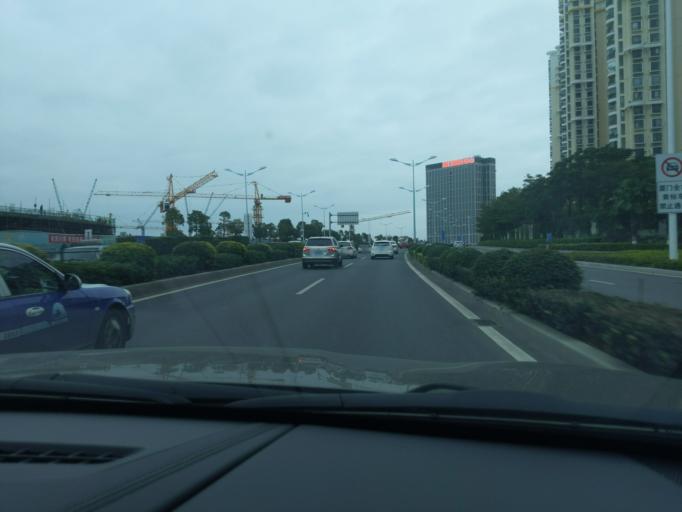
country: CN
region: Fujian
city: Liuwudian
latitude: 24.5115
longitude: 118.1827
